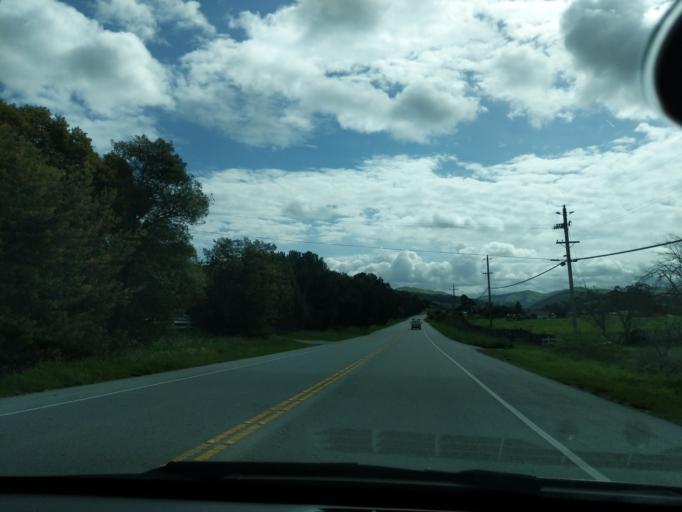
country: US
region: California
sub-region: San Benito County
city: Aromas
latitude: 36.8588
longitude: -121.6494
